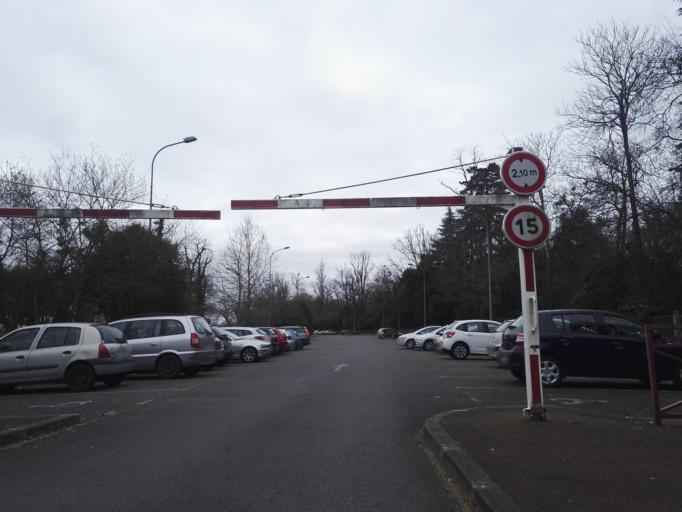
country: FR
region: Aquitaine
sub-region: Departement de la Gironde
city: Talence
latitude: 44.7922
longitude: -0.5823
